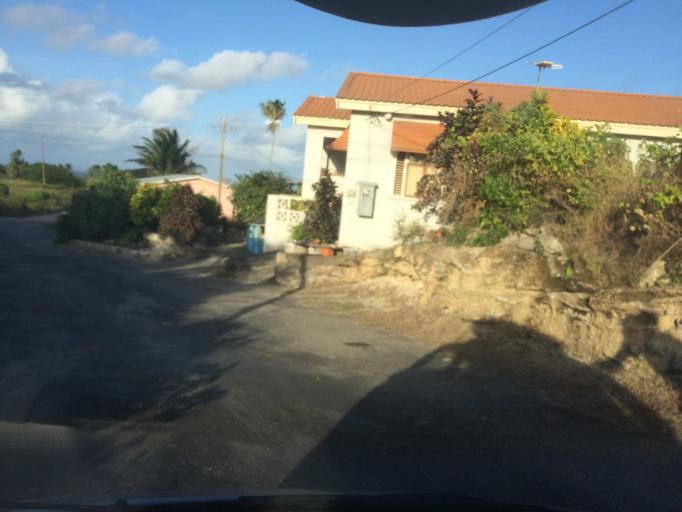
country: BB
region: Saint Lucy
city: Checker Hall
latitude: 13.3287
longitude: -59.6137
